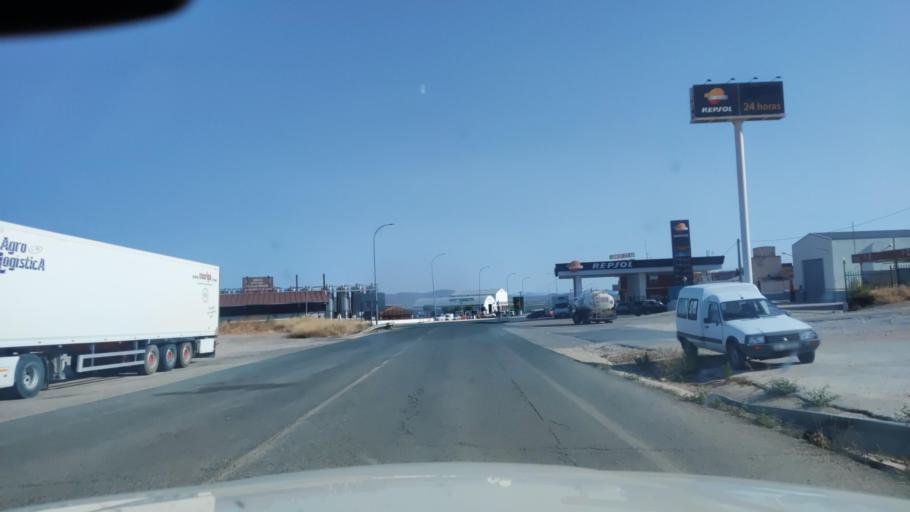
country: ES
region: Castille-La Mancha
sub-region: Provincia de Albacete
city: Tobarra
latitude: 38.6032
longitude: -1.6811
